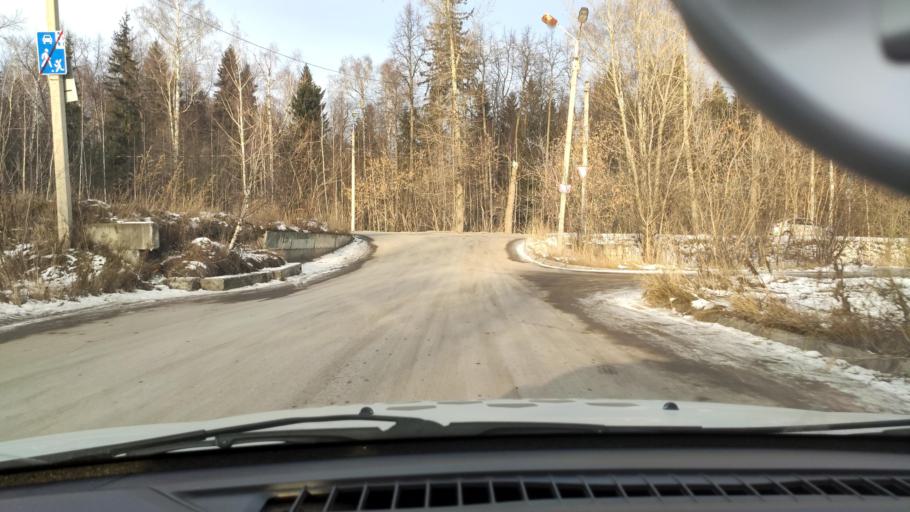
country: RU
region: Perm
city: Kondratovo
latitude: 58.0446
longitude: 56.0802
